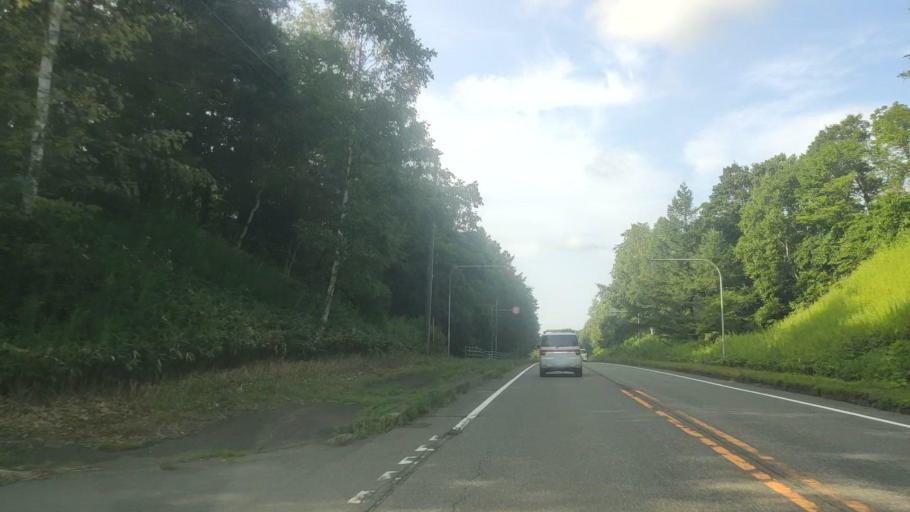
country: JP
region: Hokkaido
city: Chitose
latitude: 42.8706
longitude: 141.8225
